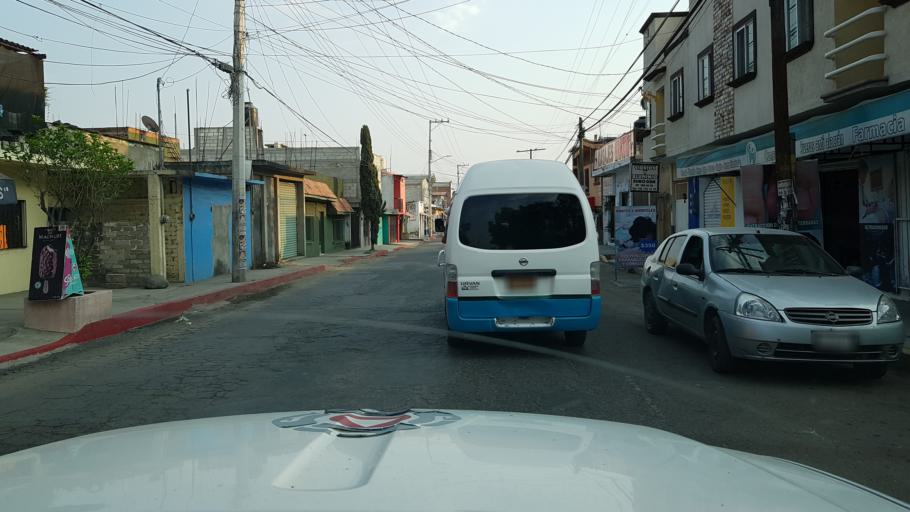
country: MX
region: Morelos
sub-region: Ayala
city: Ciudad Ayala
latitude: 18.7751
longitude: -98.9820
